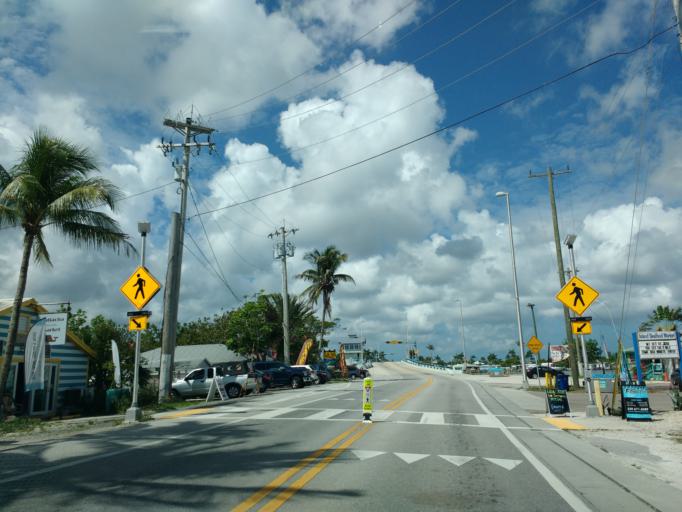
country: US
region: Florida
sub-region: Lee County
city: Pine Island Center
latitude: 26.6340
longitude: -82.0665
